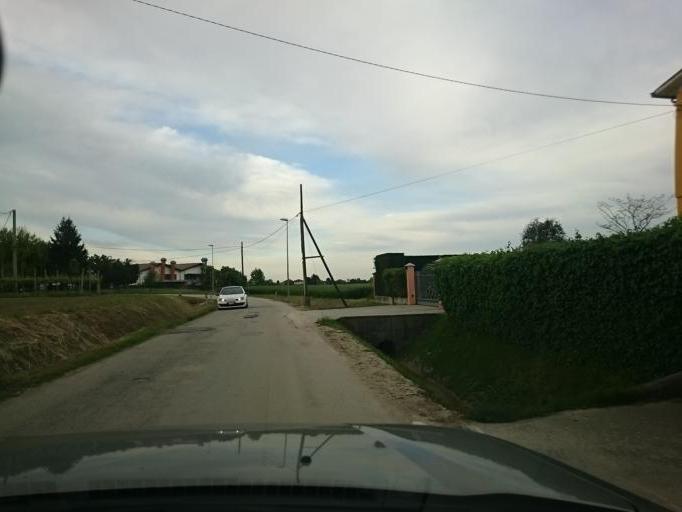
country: IT
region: Veneto
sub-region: Provincia di Padova
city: Due Carrare
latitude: 45.2841
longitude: 11.8392
